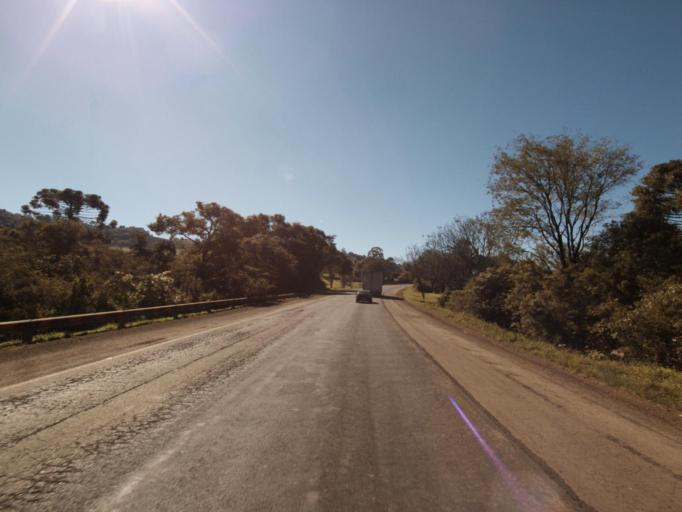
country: BR
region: Rio Grande do Sul
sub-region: Frederico Westphalen
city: Frederico Westphalen
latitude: -26.8946
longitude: -53.1895
